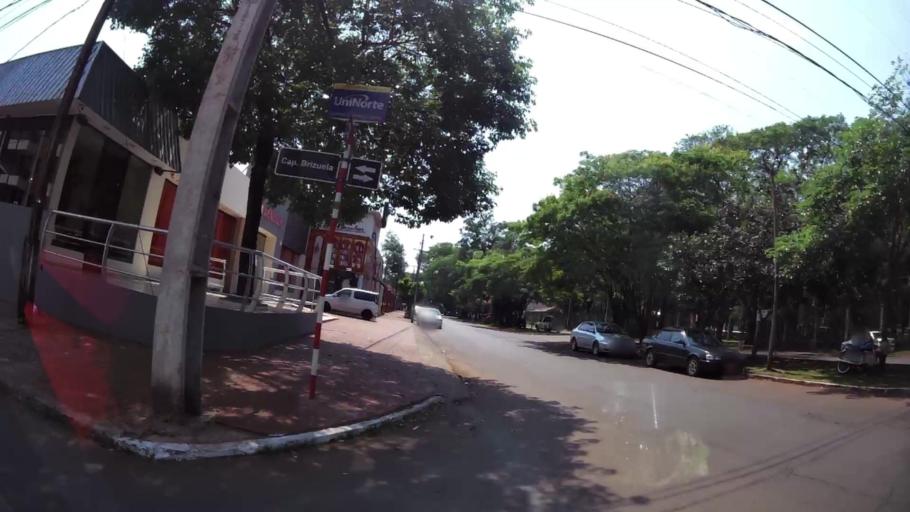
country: PY
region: Alto Parana
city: Presidente Franco
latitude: -25.5213
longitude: -54.6158
